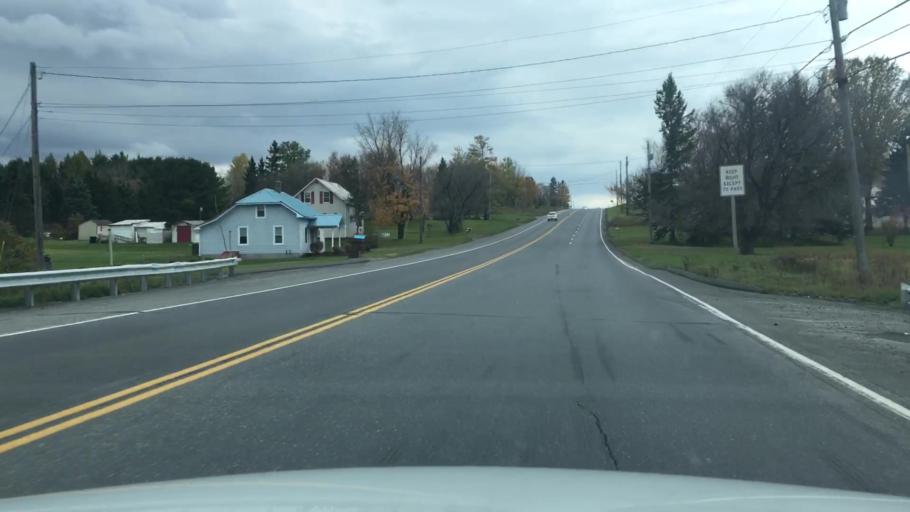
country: US
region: Maine
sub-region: Aroostook County
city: Caribou
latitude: 46.7834
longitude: -67.9890
